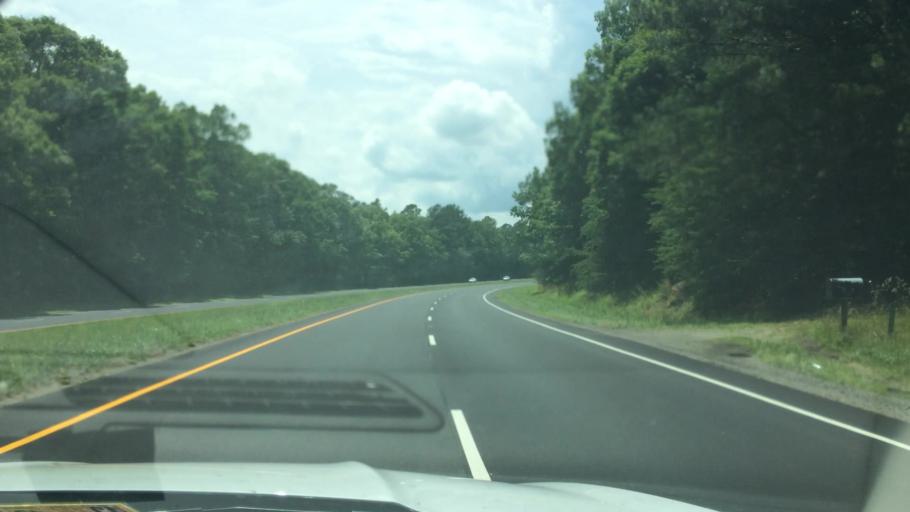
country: US
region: Virginia
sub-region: King William County
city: West Point
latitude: 37.5449
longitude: -76.6914
